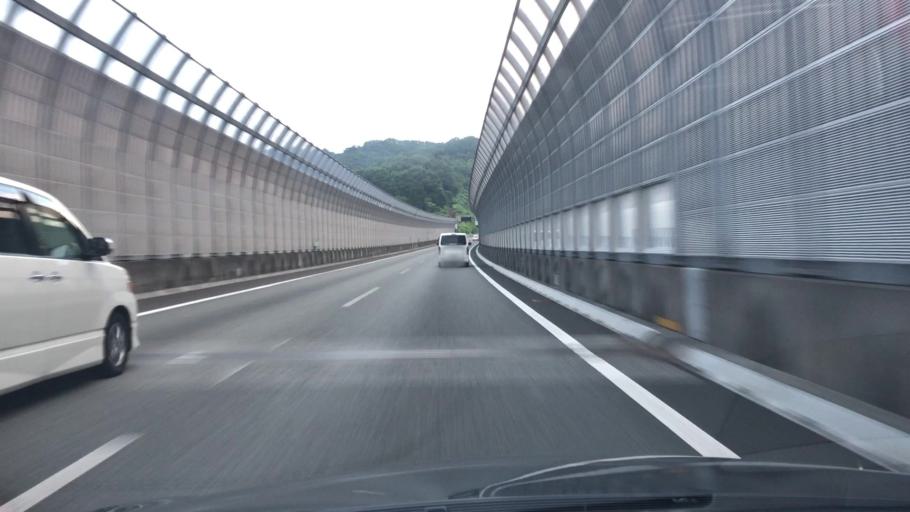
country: JP
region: Tokyo
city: Itsukaichi
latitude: 35.6972
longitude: 139.2694
